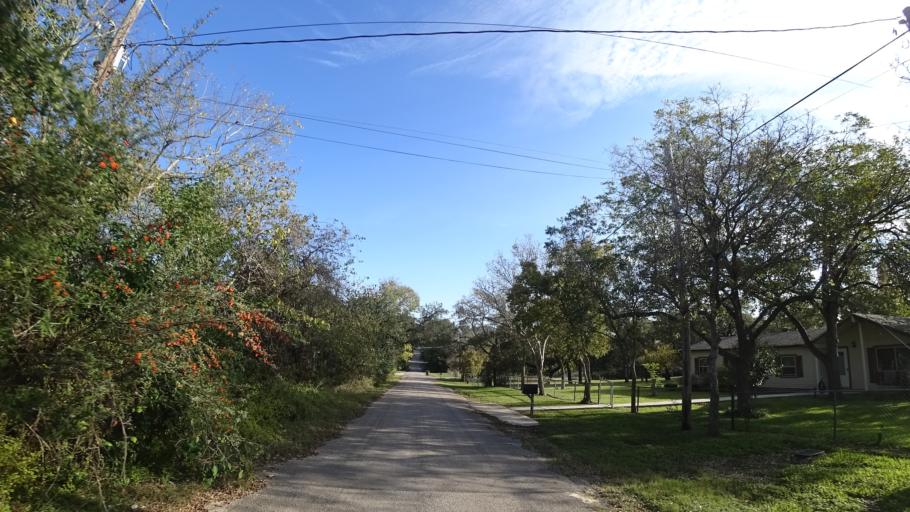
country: US
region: Texas
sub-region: Travis County
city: Barton Creek
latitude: 30.2473
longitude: -97.9206
